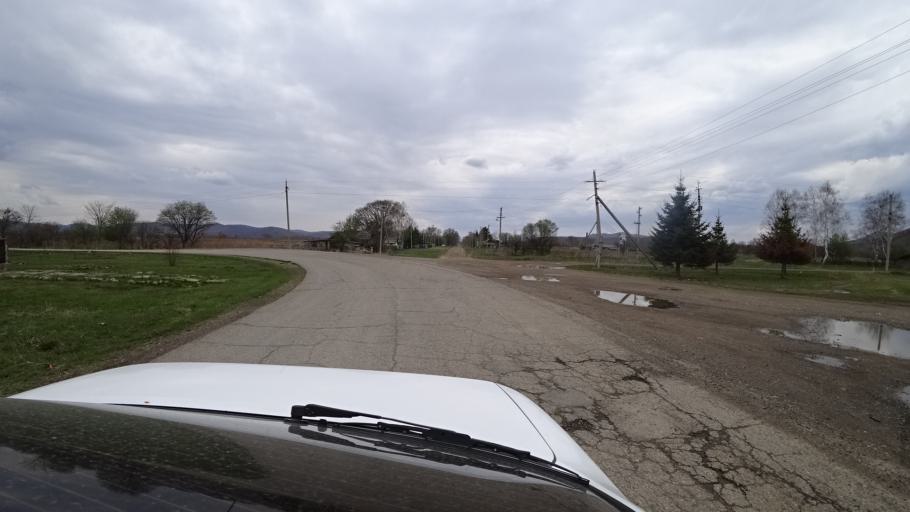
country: RU
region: Primorskiy
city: Novopokrovka
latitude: 45.5780
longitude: 134.3128
